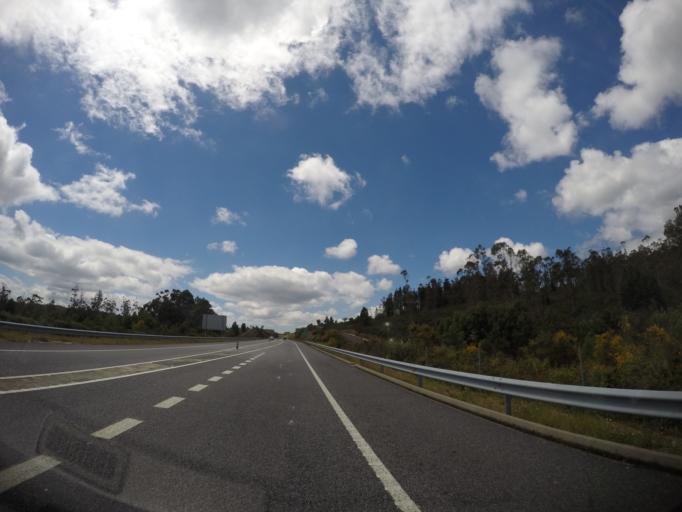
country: ES
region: Aragon
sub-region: Provincia de Zaragoza
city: Monegrillo
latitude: 41.5357
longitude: -0.4008
